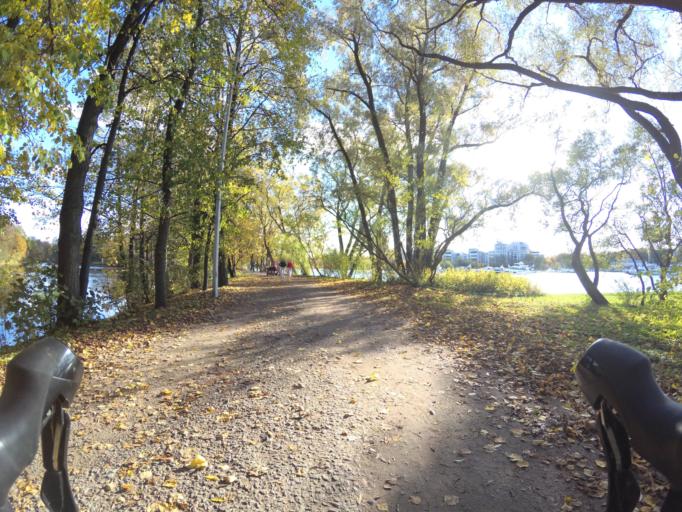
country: RU
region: St.-Petersburg
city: Staraya Derevnya
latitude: 59.9792
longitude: 30.2471
